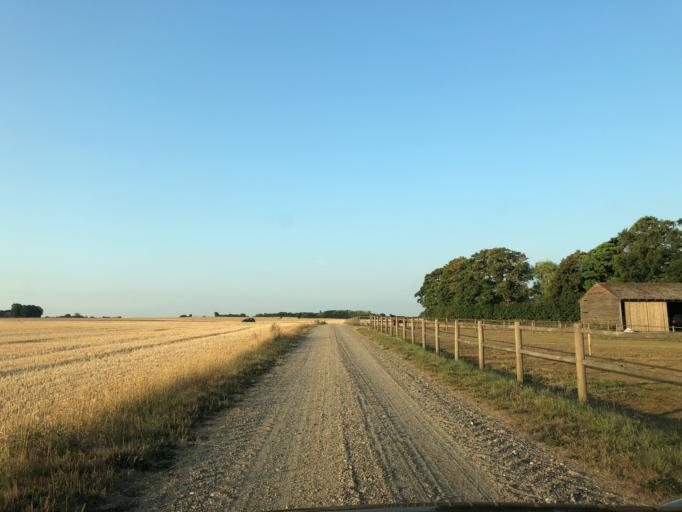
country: DK
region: Central Jutland
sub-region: Skanderborg Kommune
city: Skanderborg
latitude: 56.0891
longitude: 9.8715
